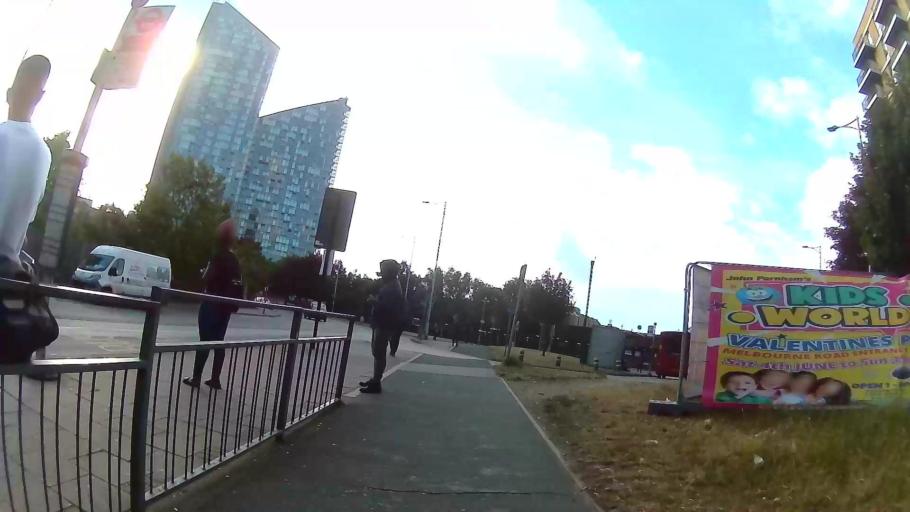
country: GB
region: England
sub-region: Greater London
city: Ilford
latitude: 51.5573
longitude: 0.0679
